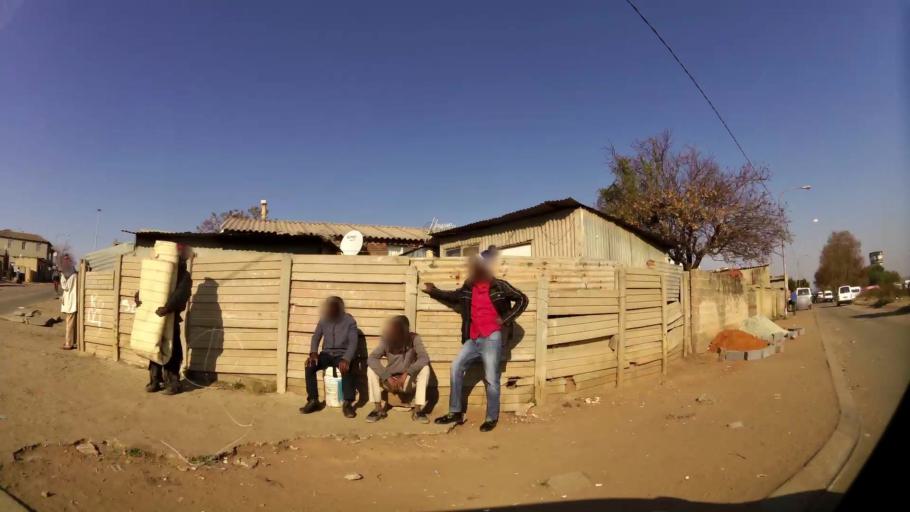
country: ZA
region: Gauteng
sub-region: City of Johannesburg Metropolitan Municipality
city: Soweto
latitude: -26.2551
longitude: 27.9387
